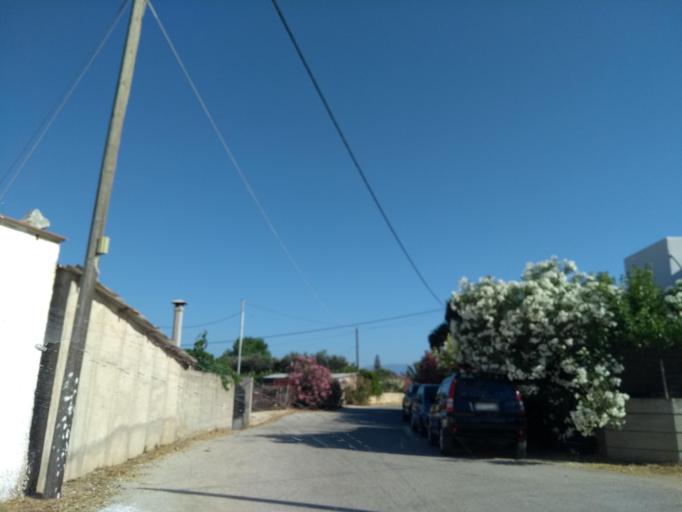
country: GR
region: Crete
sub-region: Nomos Chanias
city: Pithari
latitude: 35.5884
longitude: 24.0918
